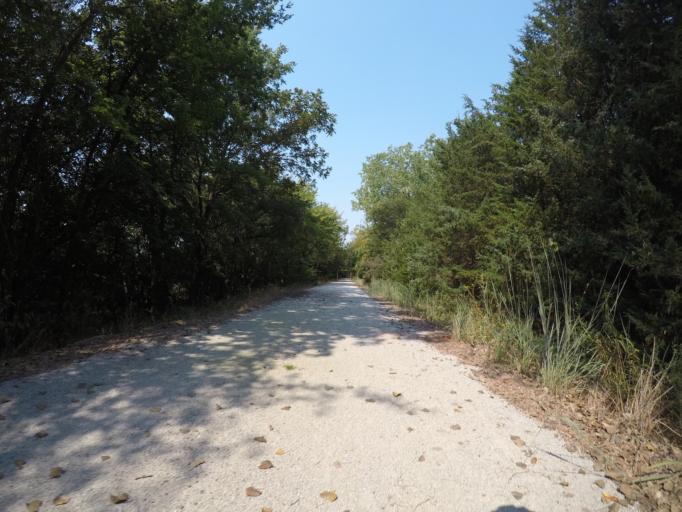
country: US
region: Nebraska
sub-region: Gage County
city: Beatrice
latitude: 40.2532
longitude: -96.7295
